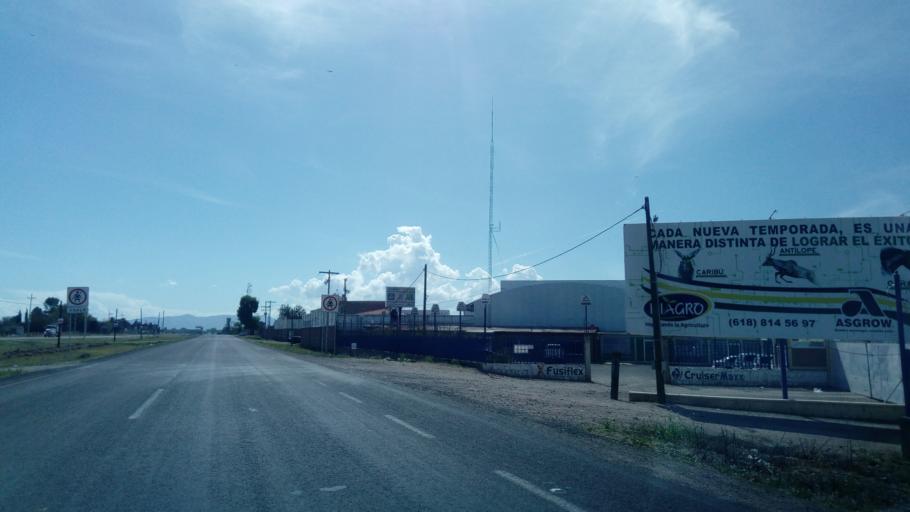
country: MX
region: Durango
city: Victoria de Durango
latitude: 24.0846
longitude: -104.5610
